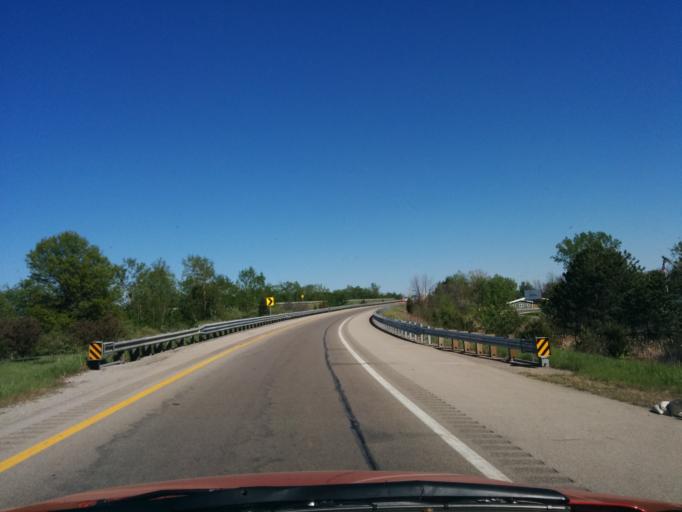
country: US
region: Michigan
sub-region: Midland County
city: Midland
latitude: 43.6108
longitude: -84.1699
